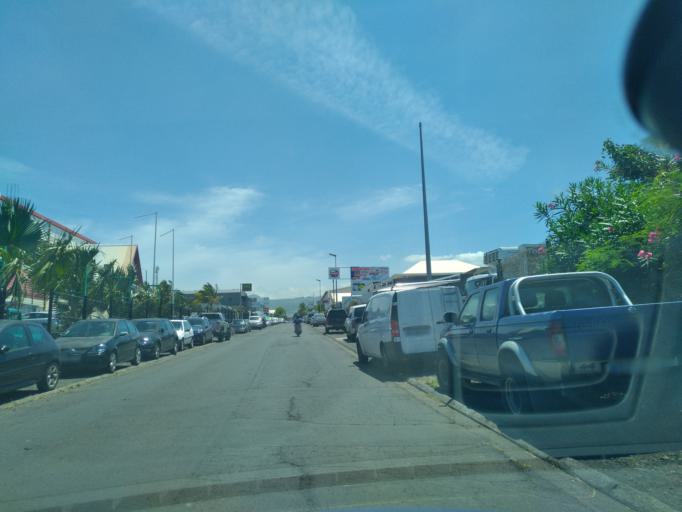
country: RE
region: Reunion
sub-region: Reunion
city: Saint-Pierre
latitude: -21.3180
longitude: 55.4525
